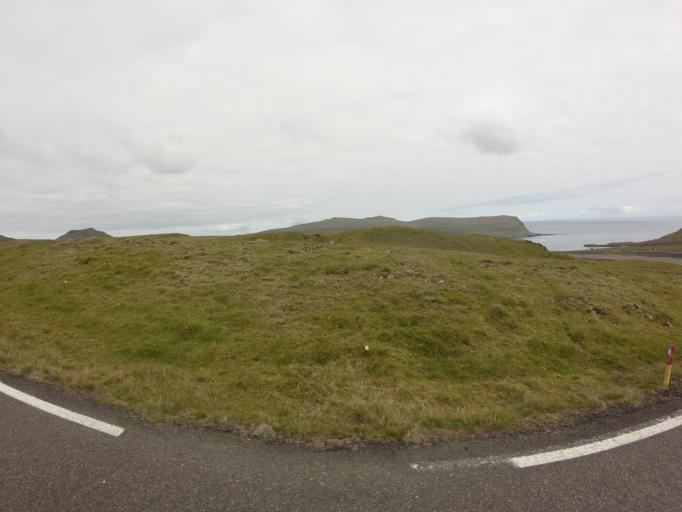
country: FO
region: Suduroy
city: Tvoroyri
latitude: 61.5227
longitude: -6.8255
